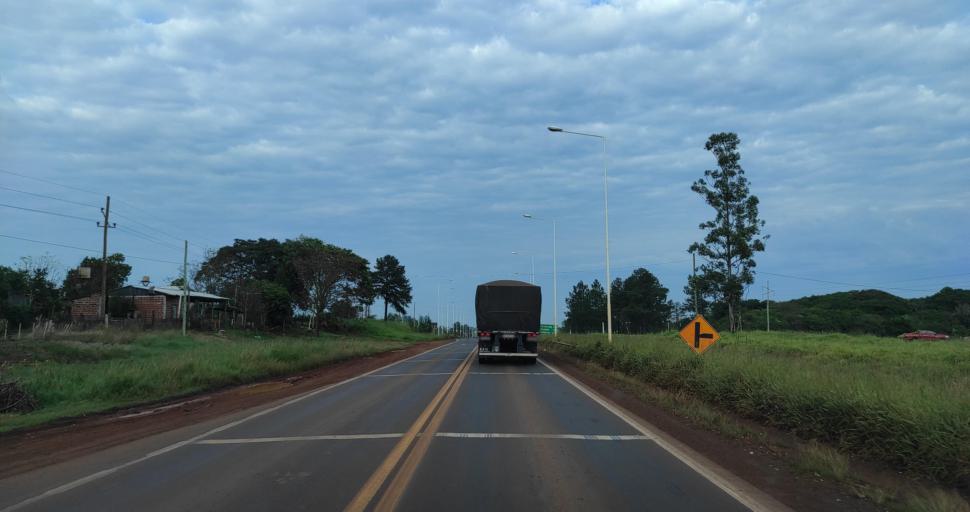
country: AR
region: Corrientes
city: Gobernador Ingeniero Valentin Virasoro
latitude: -27.9652
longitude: -56.0067
